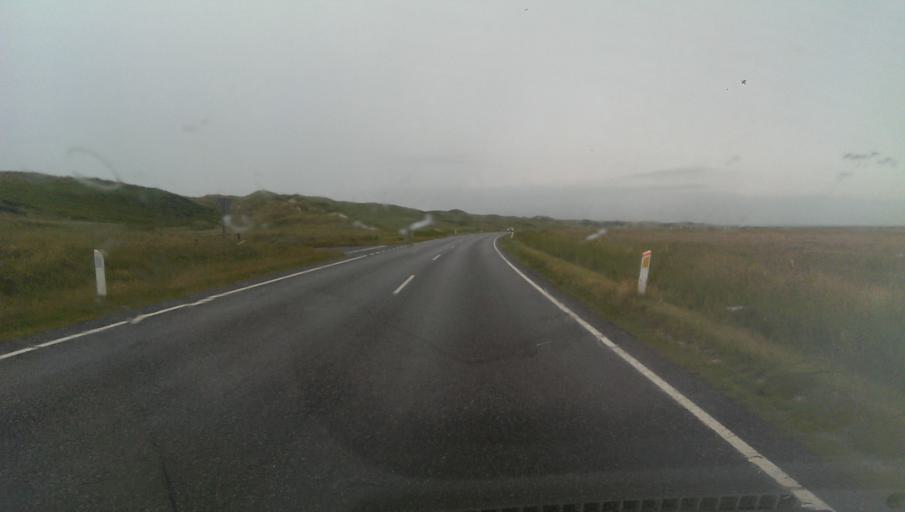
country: DK
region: Central Jutland
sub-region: Ringkobing-Skjern Kommune
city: Ringkobing
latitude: 56.1841
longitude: 8.1266
